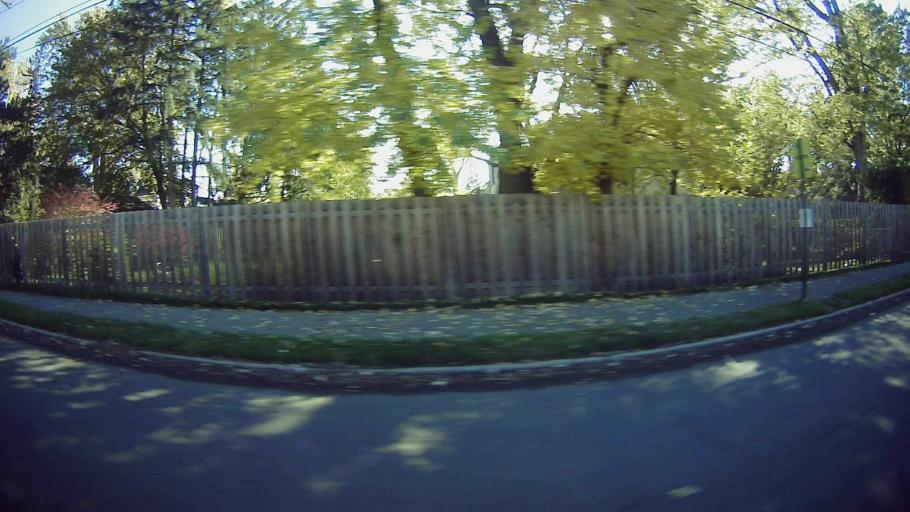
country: US
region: Michigan
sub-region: Oakland County
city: Ferndale
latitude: 42.4317
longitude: -83.1343
